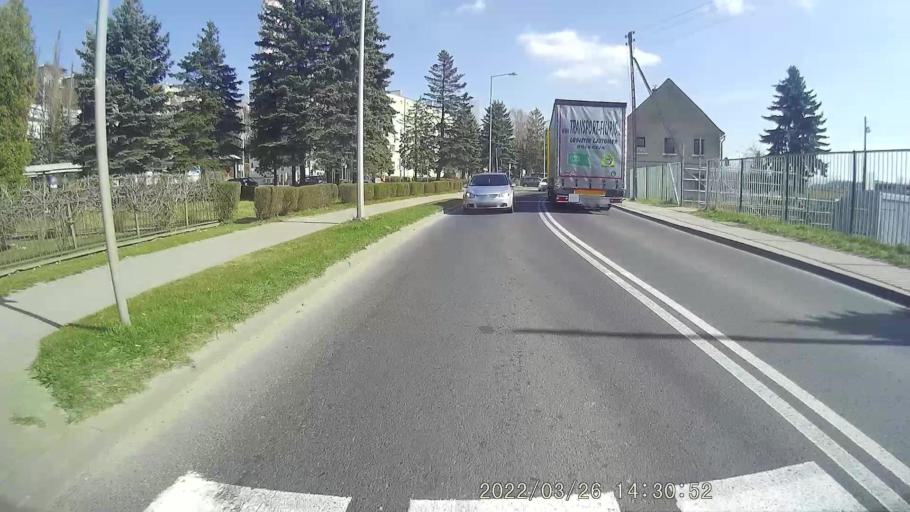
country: DE
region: Saxony
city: Hirschfelde
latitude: 50.9469
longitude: 14.9039
